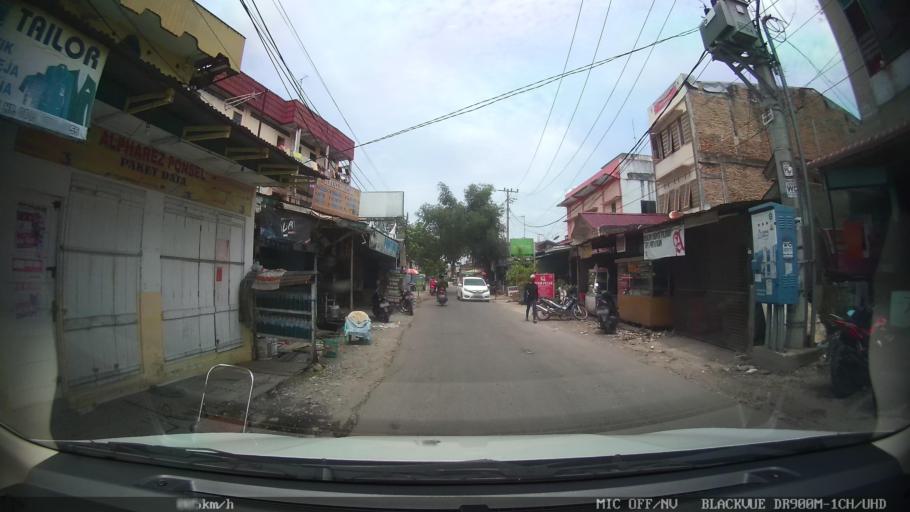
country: ID
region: North Sumatra
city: Medan
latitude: 3.5549
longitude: 98.6611
